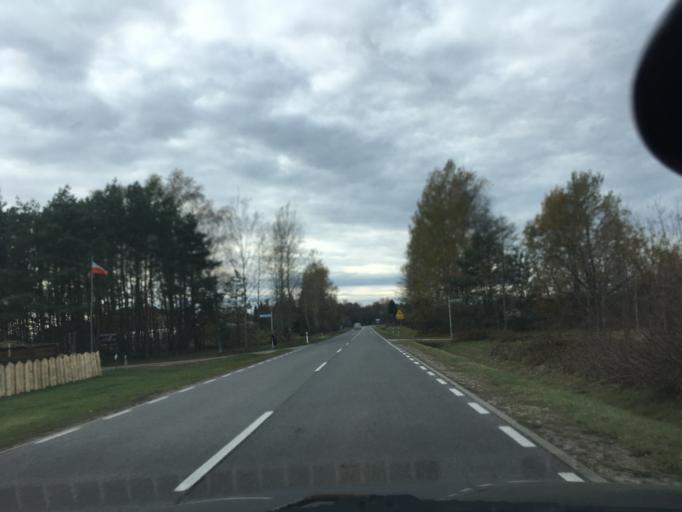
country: PL
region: Masovian Voivodeship
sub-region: Powiat piaseczynski
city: Tarczyn
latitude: 51.9802
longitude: 20.8974
